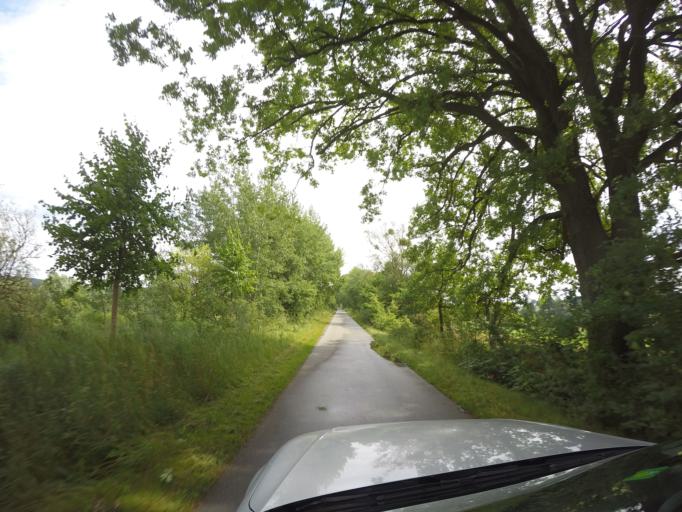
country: DE
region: Mecklenburg-Vorpommern
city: Wesenberg
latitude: 53.3625
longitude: 12.8806
